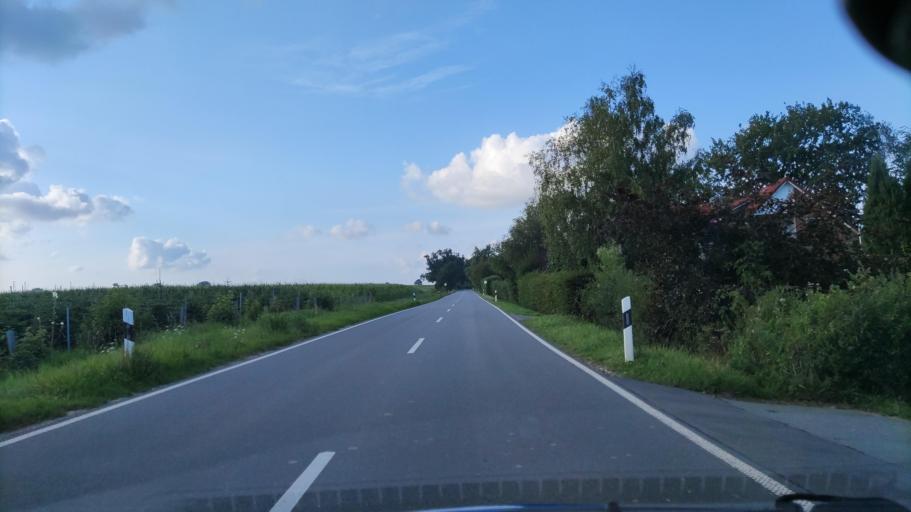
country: DE
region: Schleswig-Holstein
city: Glasau
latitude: 54.0443
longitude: 10.5322
